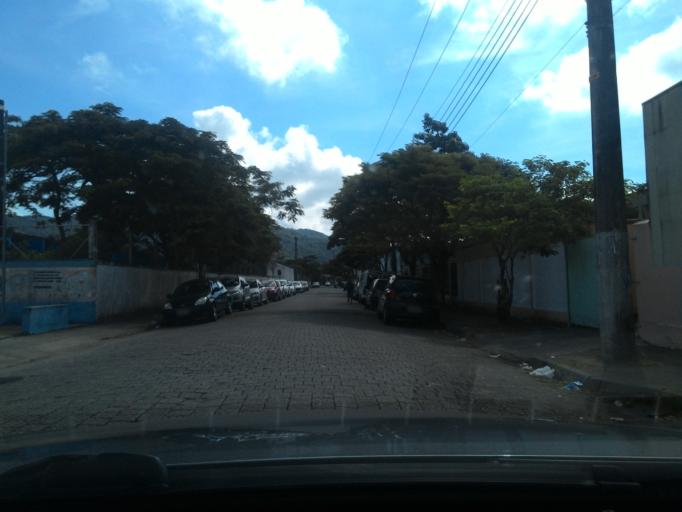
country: BR
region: Sao Paulo
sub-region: Iguape
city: Iguape
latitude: -24.7111
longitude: -47.5600
